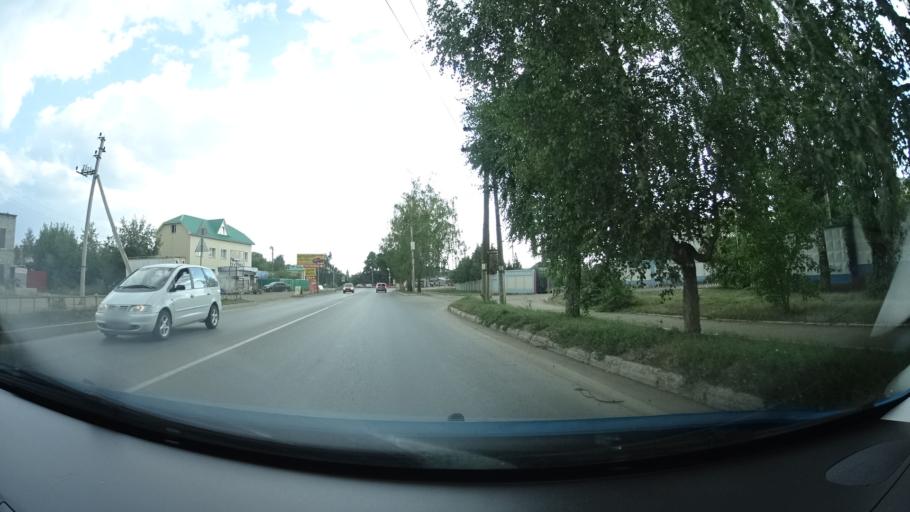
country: RU
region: Bashkortostan
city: Oktyabr'skiy
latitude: 54.4915
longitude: 53.4476
